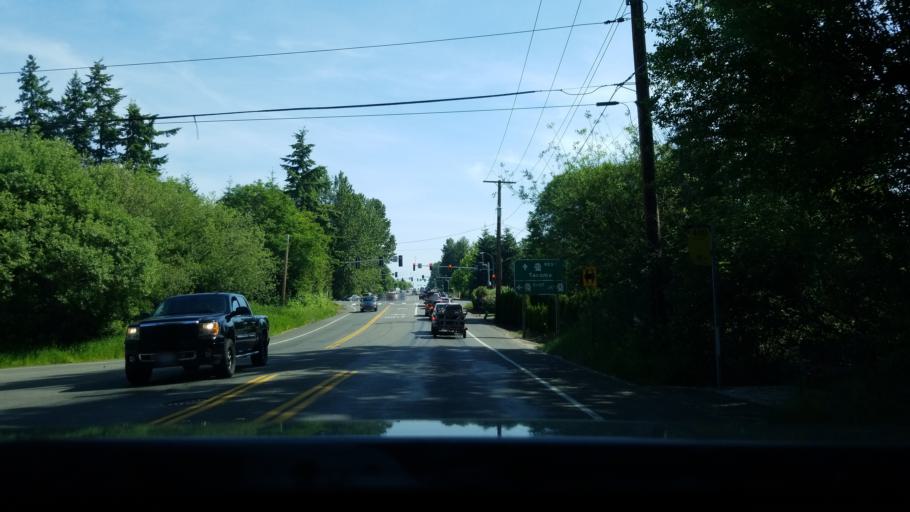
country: US
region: Washington
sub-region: Pierce County
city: Puyallup
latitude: 47.1632
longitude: -122.3042
